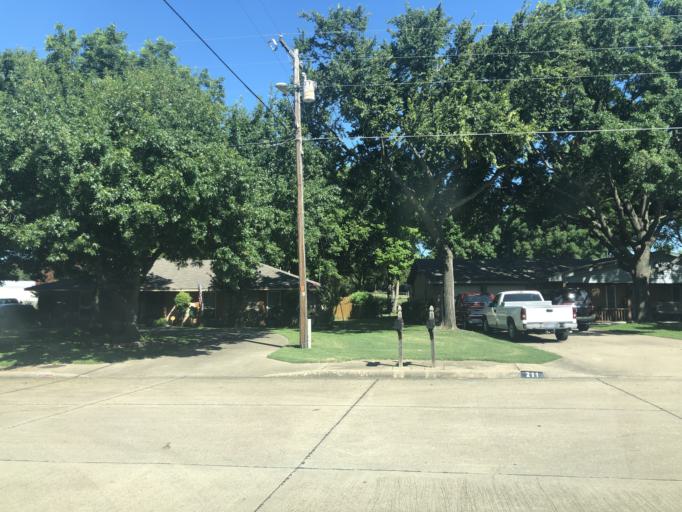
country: US
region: Texas
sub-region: Dallas County
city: Duncanville
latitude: 32.6486
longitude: -96.9385
